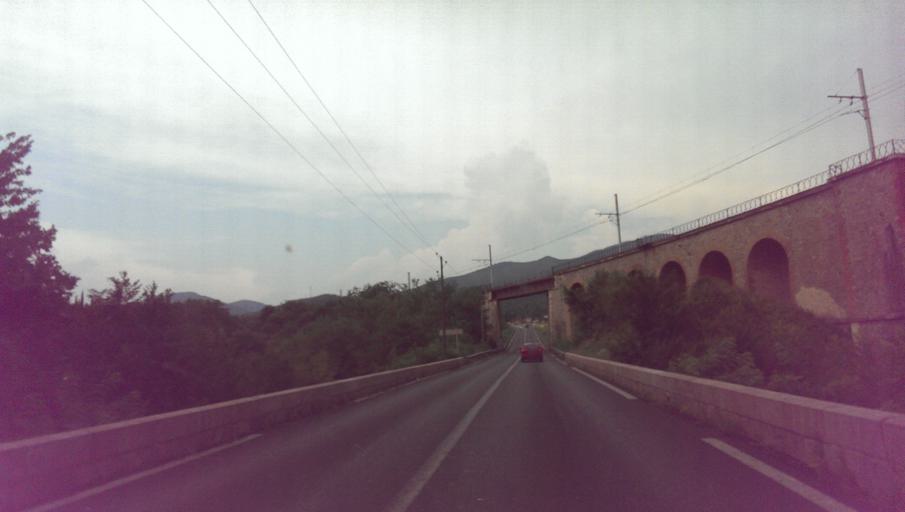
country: FR
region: Languedoc-Roussillon
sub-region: Departement des Pyrenees-Orientales
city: Vinca
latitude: 42.6503
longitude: 2.5553
